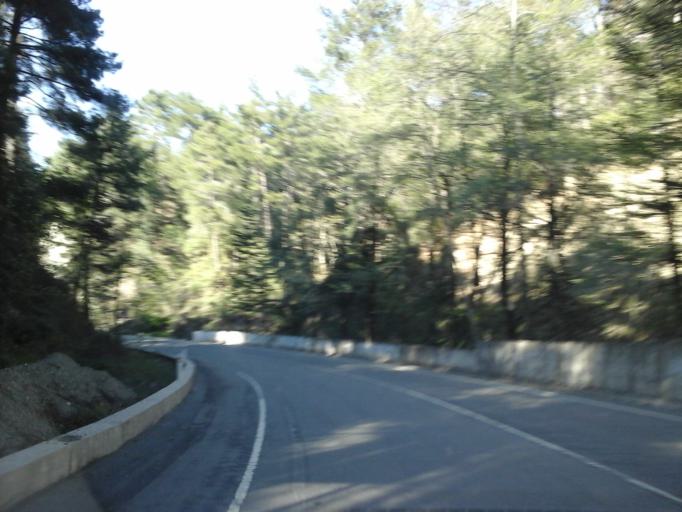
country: CY
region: Limassol
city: Kyperounta
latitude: 34.9462
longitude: 32.9295
